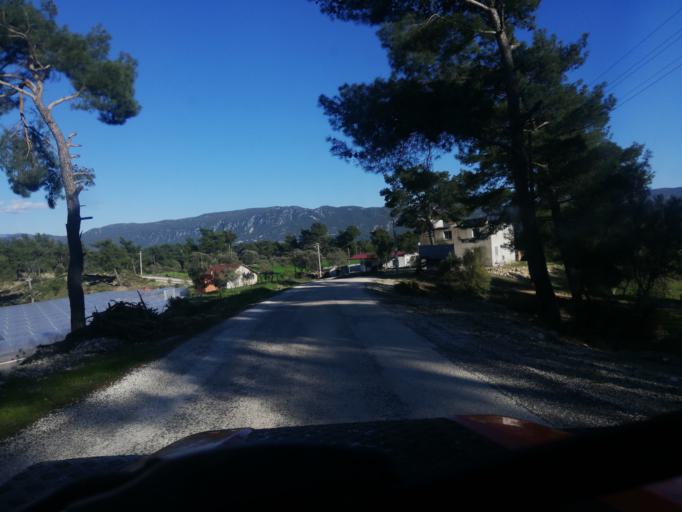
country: TR
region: Antalya
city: Kas
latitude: 36.2979
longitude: 29.6999
